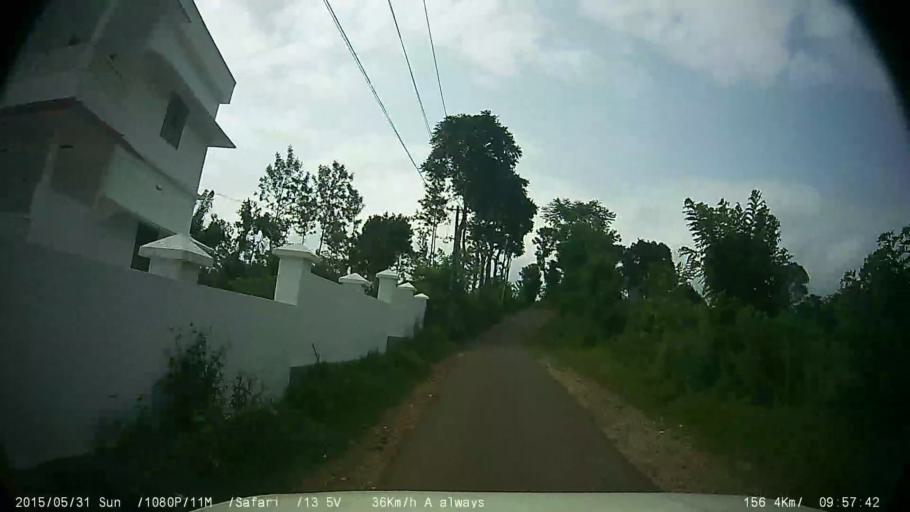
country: IN
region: Kerala
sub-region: Wayanad
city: Kalpetta
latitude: 11.5931
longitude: 76.0590
